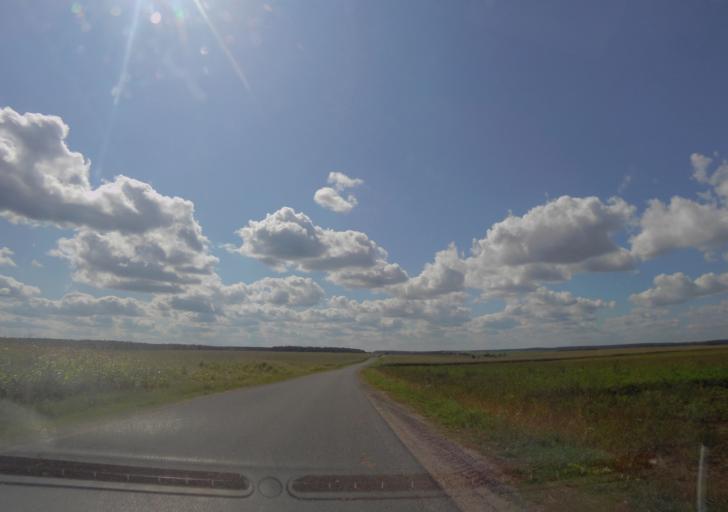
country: BY
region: Minsk
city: Horad Barysaw
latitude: 54.3830
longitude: 28.4806
